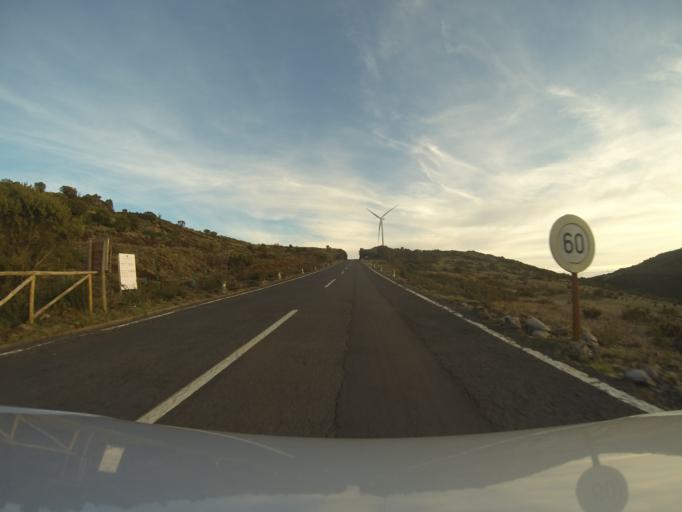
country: PT
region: Madeira
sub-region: Sao Vicente
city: Sao Vicente
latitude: 32.7515
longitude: -17.0583
